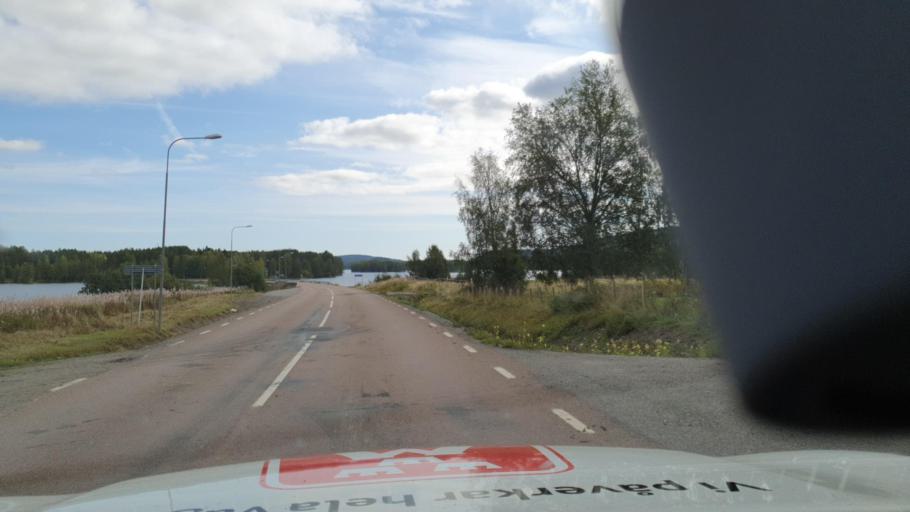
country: SE
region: Jaemtland
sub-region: Stroemsunds Kommun
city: Stroemsund
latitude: 63.7215
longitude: 15.8163
